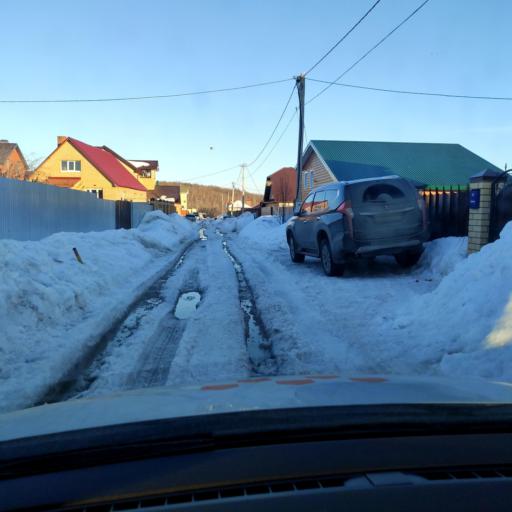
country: RU
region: Tatarstan
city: Stolbishchi
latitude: 55.7579
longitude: 49.2985
